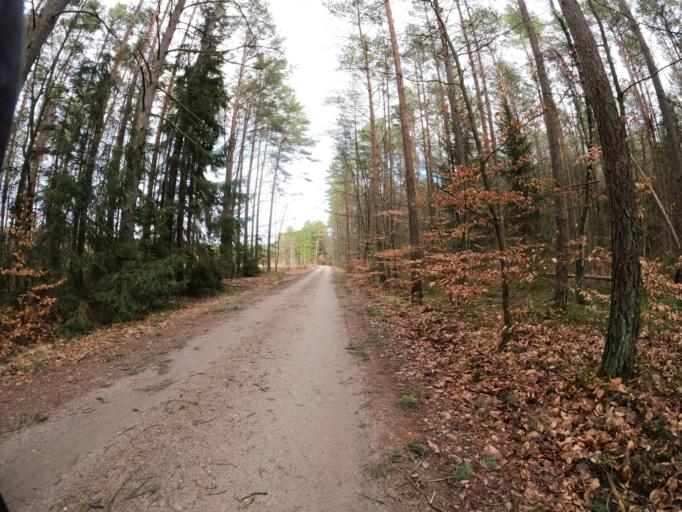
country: PL
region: Greater Poland Voivodeship
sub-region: Powiat zlotowski
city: Sypniewo
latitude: 53.4355
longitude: 16.5629
